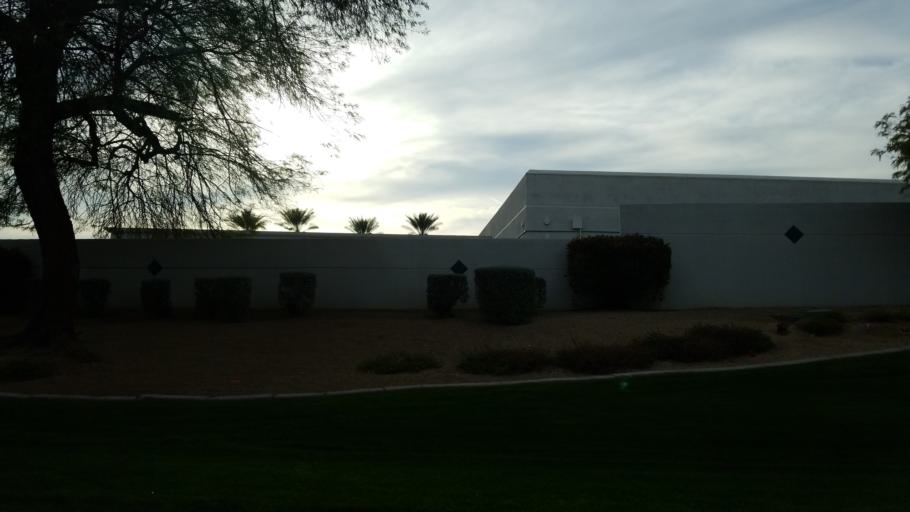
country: US
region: Arizona
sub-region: Maricopa County
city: Paradise Valley
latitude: 33.6037
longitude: -111.9759
